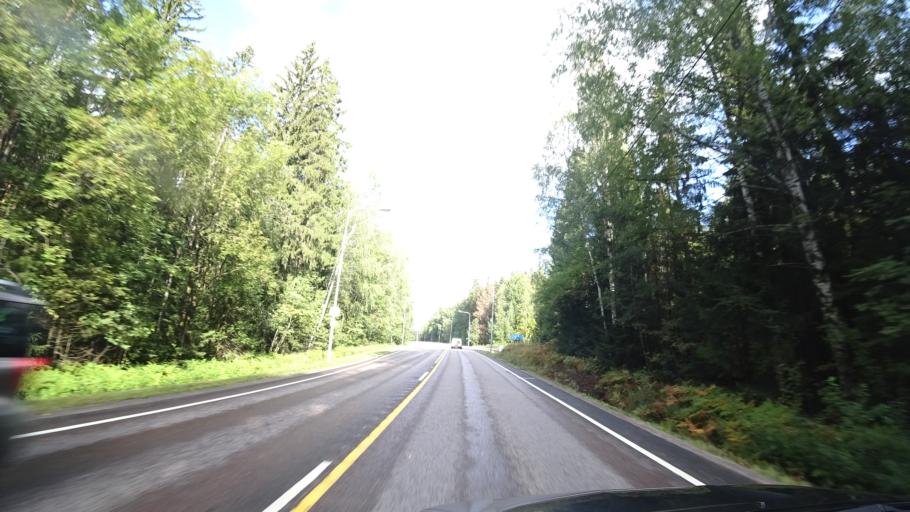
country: FI
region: Uusimaa
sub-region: Helsinki
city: Hyvinge
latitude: 60.5328
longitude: 24.9193
